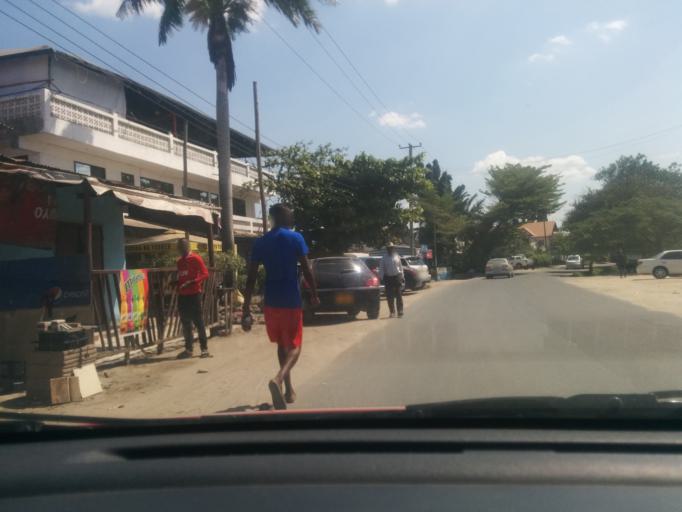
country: TZ
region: Dar es Salaam
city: Magomeni
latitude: -6.7801
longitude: 39.2207
